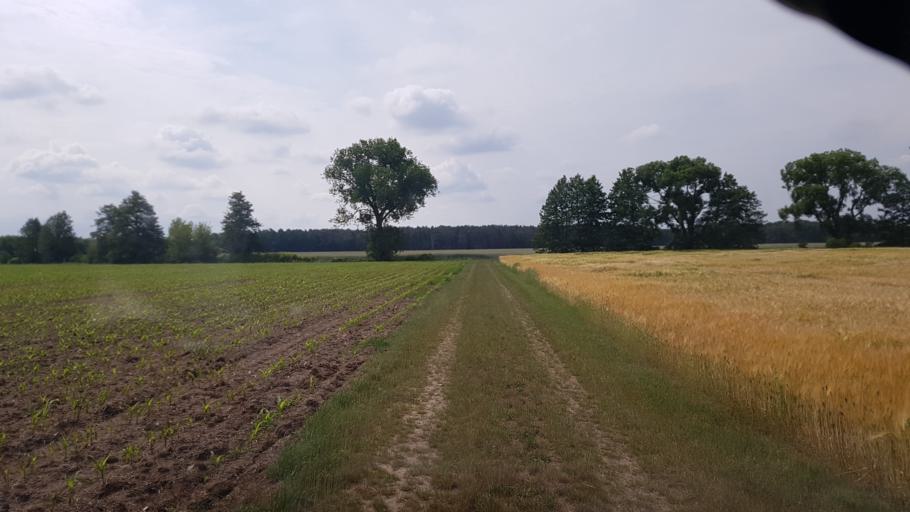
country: DE
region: Brandenburg
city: Schonewalde
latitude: 51.6512
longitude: 13.5952
